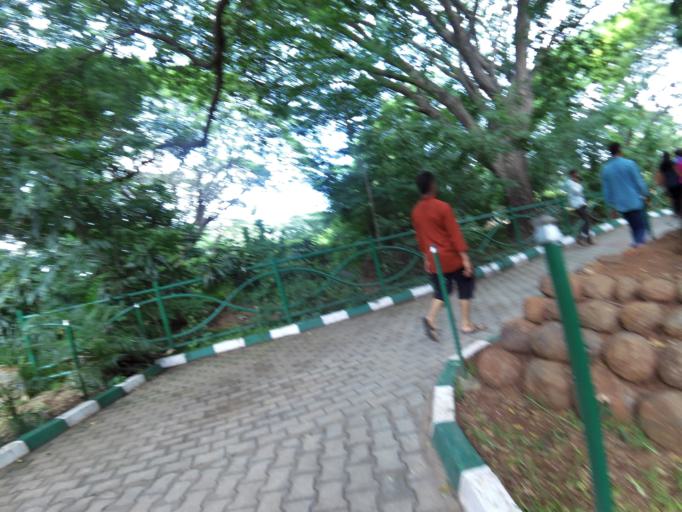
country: IN
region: Karnataka
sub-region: Mysore
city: Mysore
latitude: 12.2995
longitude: 76.6665
